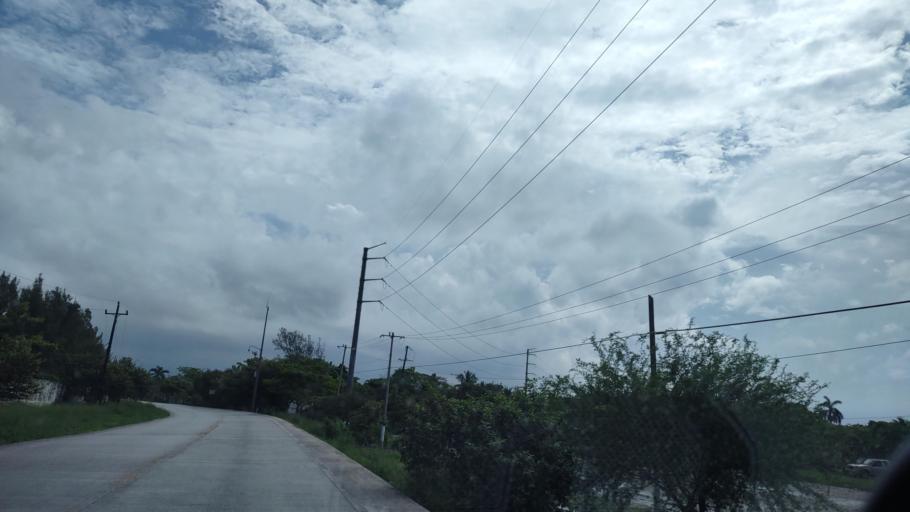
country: MX
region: Veracruz
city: Anahuac
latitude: 22.2073
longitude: -97.8668
